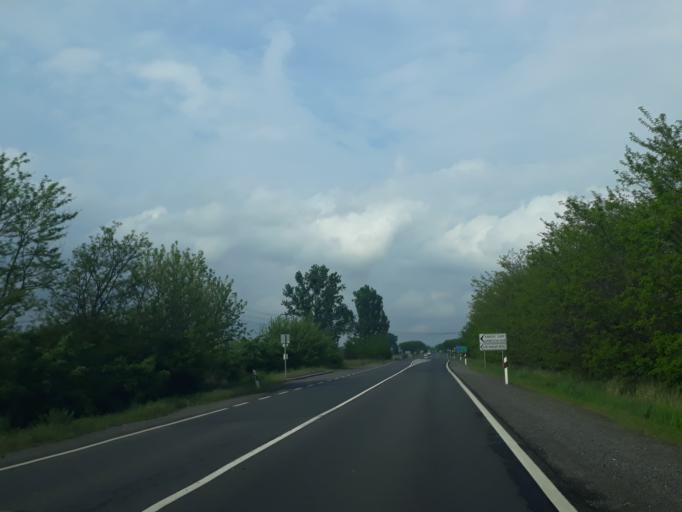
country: HU
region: Szabolcs-Szatmar-Bereg
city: Nyirtass
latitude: 48.1238
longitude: 22.0079
